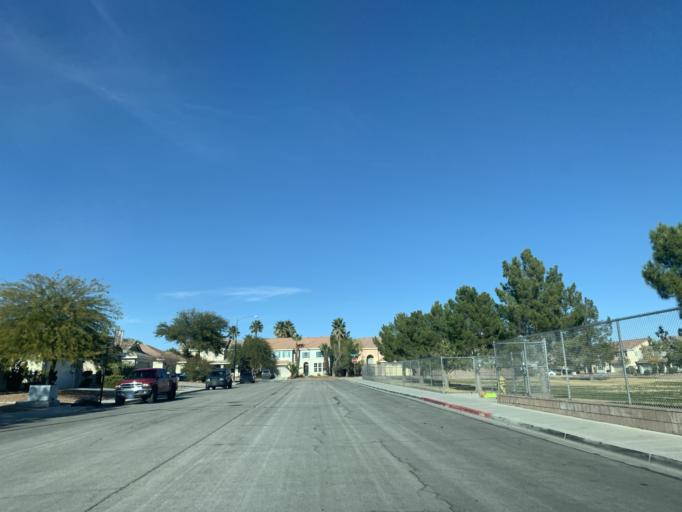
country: US
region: Nevada
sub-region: Clark County
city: Summerlin South
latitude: 36.1235
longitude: -115.3038
